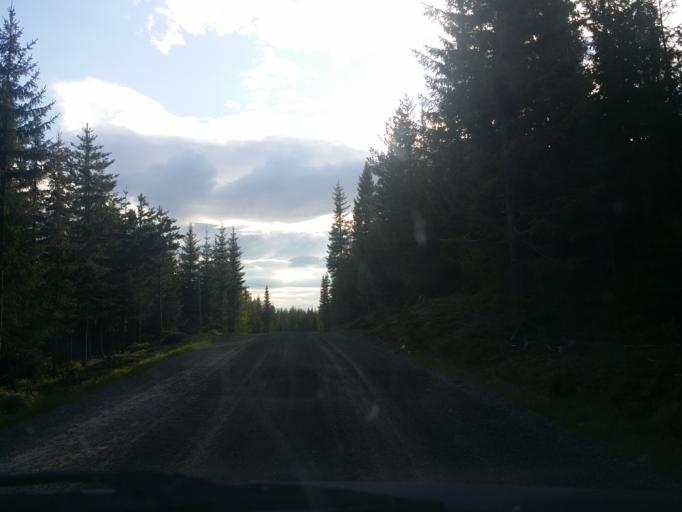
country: NO
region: Hedmark
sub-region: Ringsaker
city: Moelv
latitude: 61.0750
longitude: 10.8277
